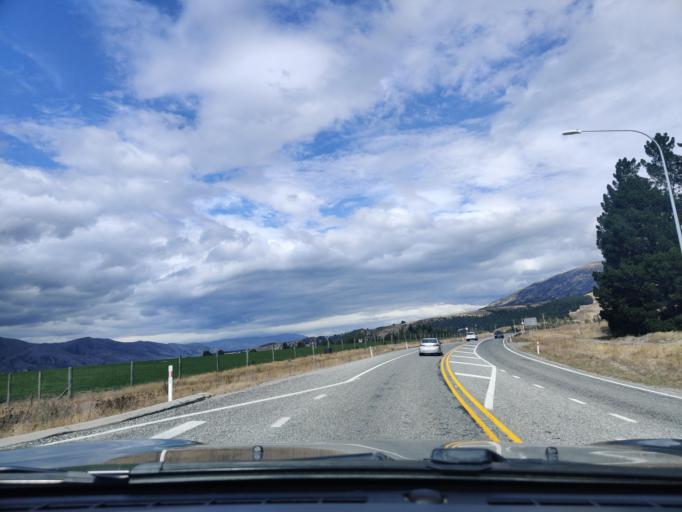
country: NZ
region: Otago
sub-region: Queenstown-Lakes District
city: Wanaka
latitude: -44.7340
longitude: 169.2592
